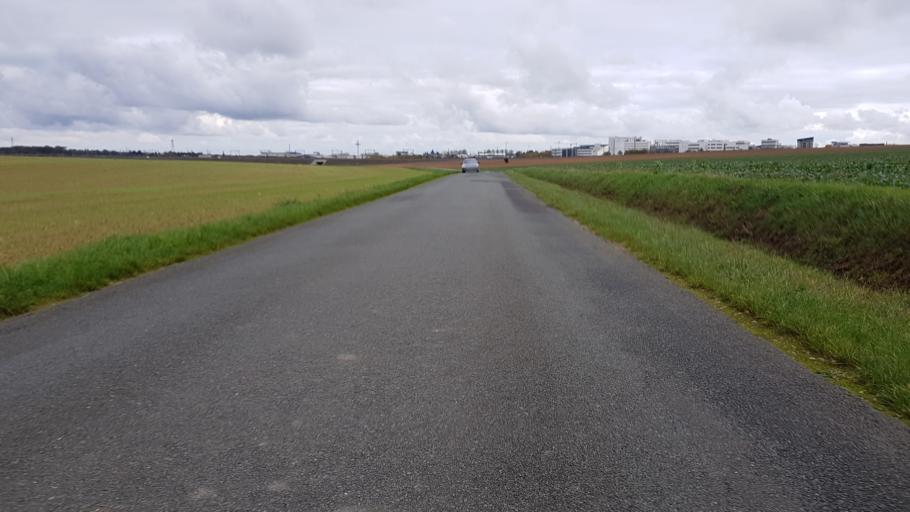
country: FR
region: Poitou-Charentes
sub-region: Departement de la Vienne
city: Chasseneuil-du-Poitou
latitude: 46.6614
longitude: 0.3464
